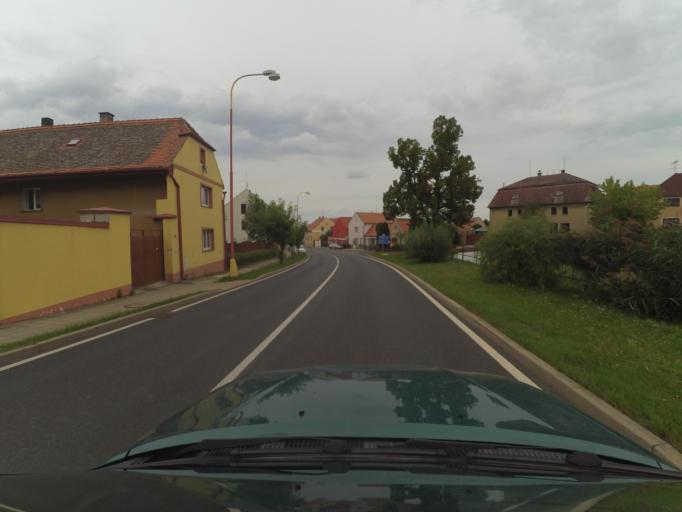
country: CZ
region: Ustecky
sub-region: Okres Louny
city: Louny
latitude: 50.3121
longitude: 13.7994
